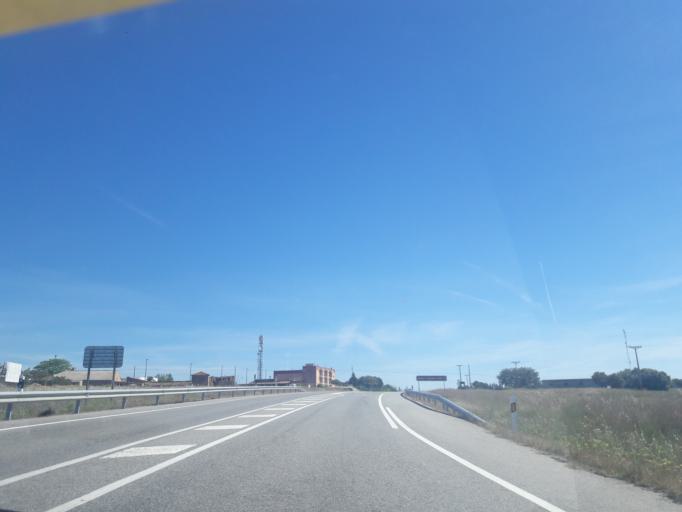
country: ES
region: Castille and Leon
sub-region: Provincia de Salamanca
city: Martinamor
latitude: 40.8084
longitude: -5.6321
